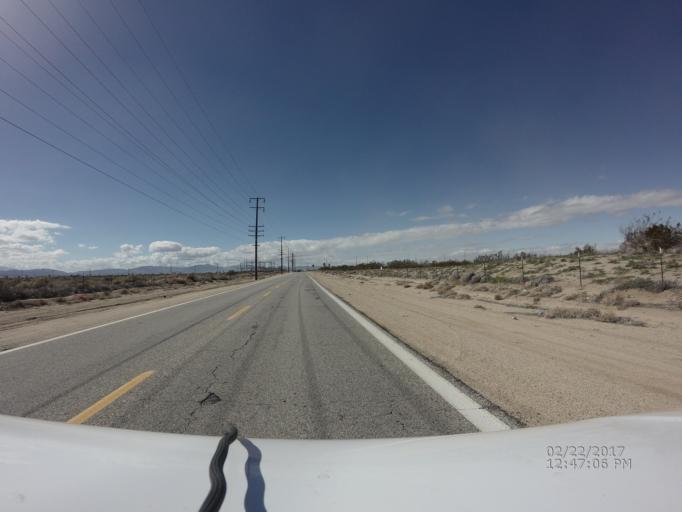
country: US
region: California
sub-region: Los Angeles County
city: Littlerock
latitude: 34.6167
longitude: -117.9654
